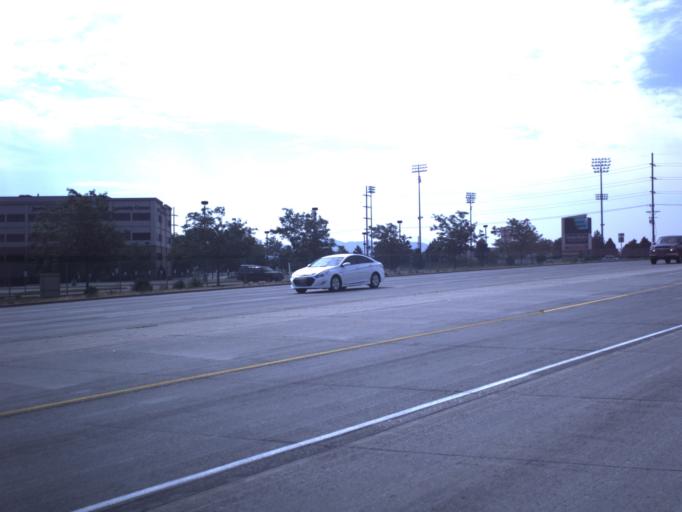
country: US
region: Utah
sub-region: Salt Lake County
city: South Jordan Heights
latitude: 40.5899
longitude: -111.9773
